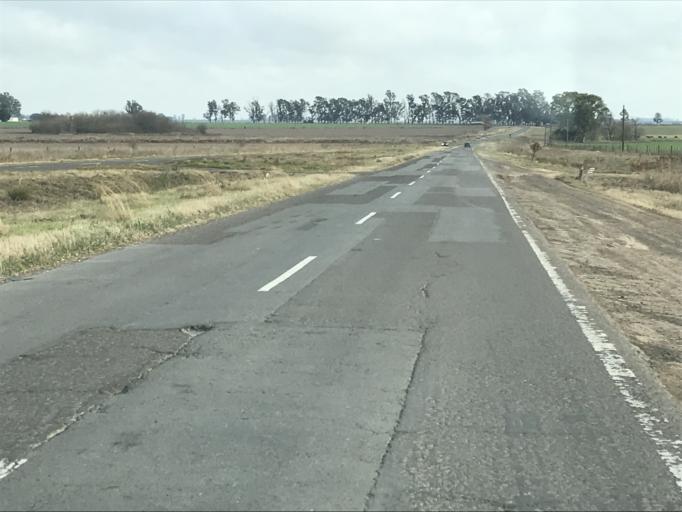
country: AR
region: Santa Fe
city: Carcarana
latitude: -32.8400
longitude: -61.2717
